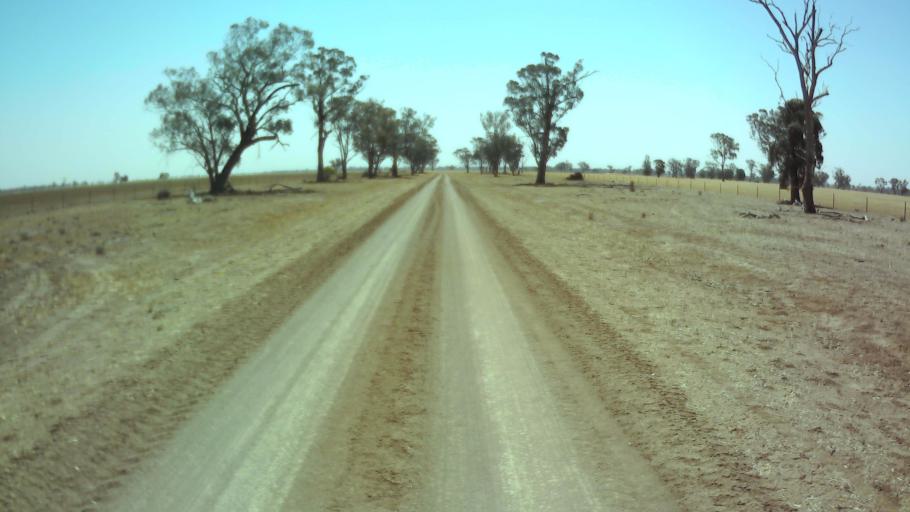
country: AU
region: New South Wales
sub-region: Weddin
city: Grenfell
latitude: -34.0041
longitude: 147.8807
